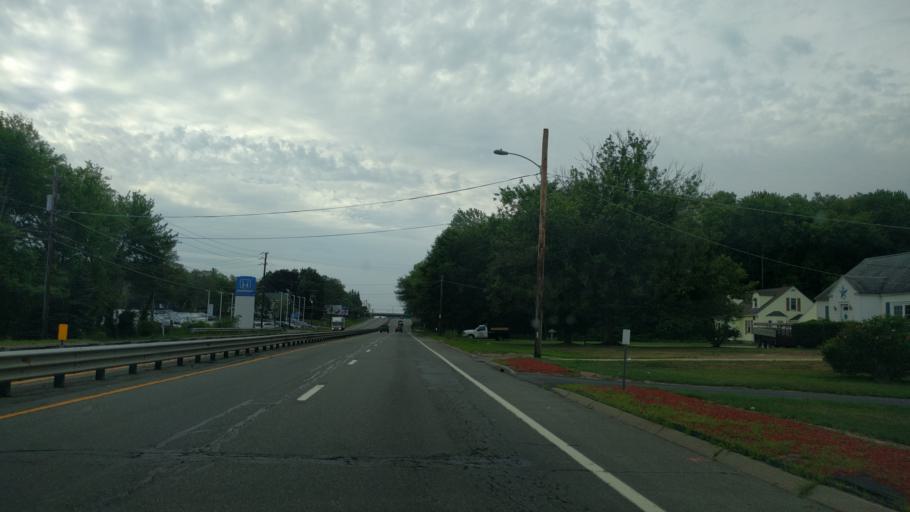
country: US
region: Rhode Island
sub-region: Providence County
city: Cumberland Hill
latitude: 41.9551
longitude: -71.4891
